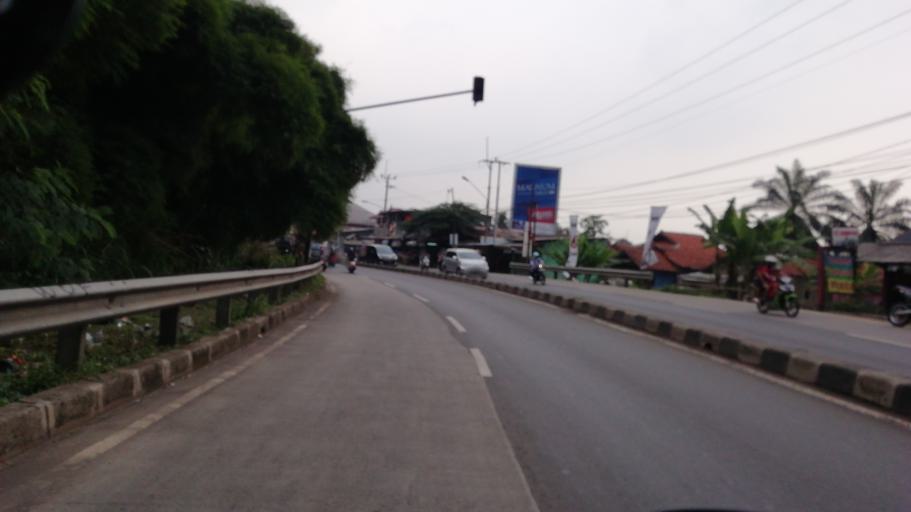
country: ID
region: West Java
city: Ciampea
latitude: -6.5160
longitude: 106.7572
